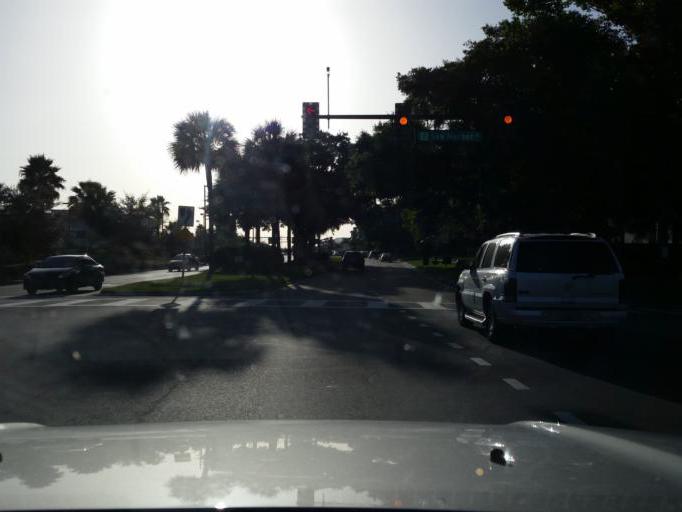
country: US
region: Florida
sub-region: Orange County
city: Williamsburg
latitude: 28.4081
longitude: -81.4689
